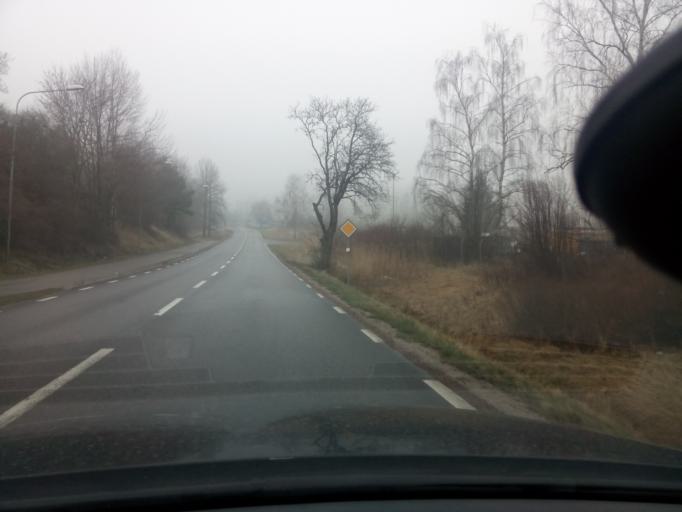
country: SE
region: Soedermanland
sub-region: Nykopings Kommun
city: Nykoping
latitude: 58.7690
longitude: 17.0293
